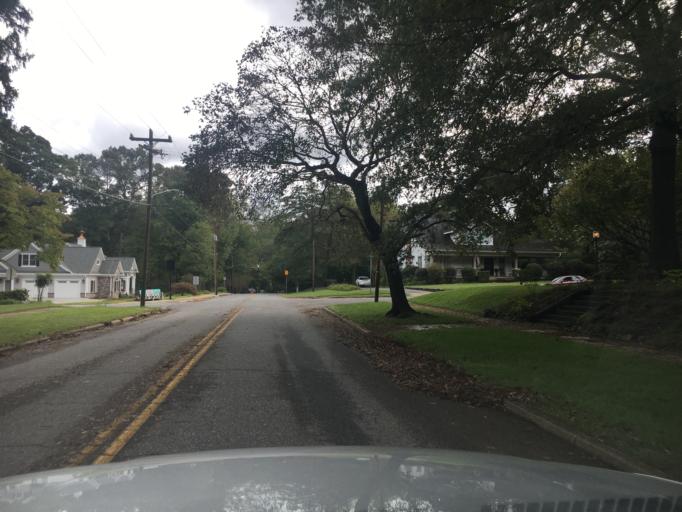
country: US
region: North Carolina
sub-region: Catawba County
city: Hickory
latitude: 35.7384
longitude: -81.3337
